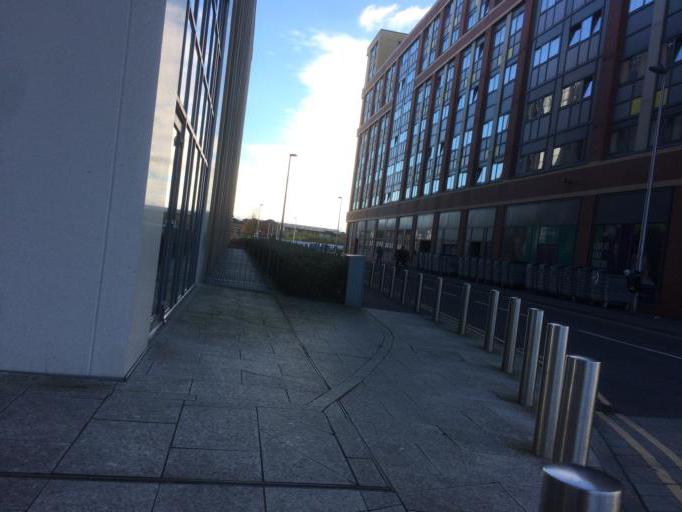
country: GB
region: Scotland
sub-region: Glasgow City
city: Glasgow
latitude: 55.8594
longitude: -4.2374
